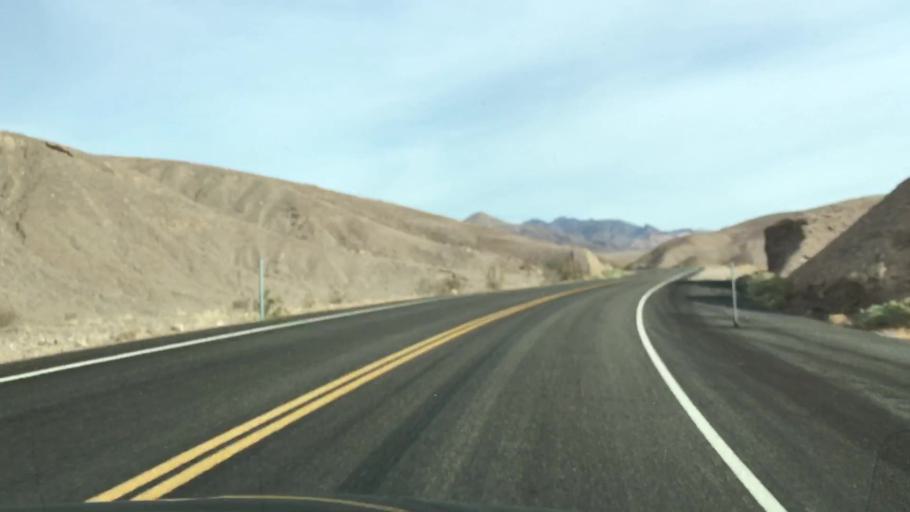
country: US
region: Nevada
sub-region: Nye County
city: Beatty
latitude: 36.6733
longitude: -117.0128
